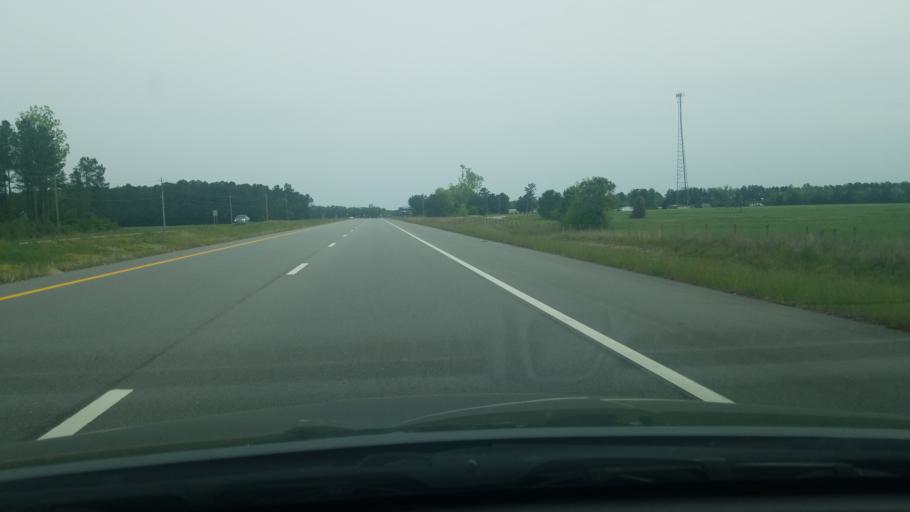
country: US
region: North Carolina
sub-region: Jones County
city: Maysville
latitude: 34.9699
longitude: -77.2400
